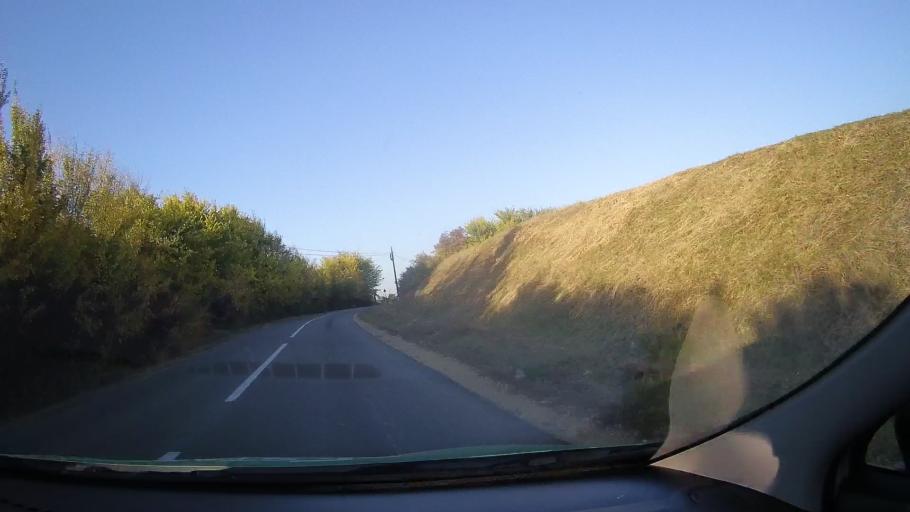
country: RO
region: Bihor
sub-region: Comuna Biharea
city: Oradea
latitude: 47.1006
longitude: 21.9263
